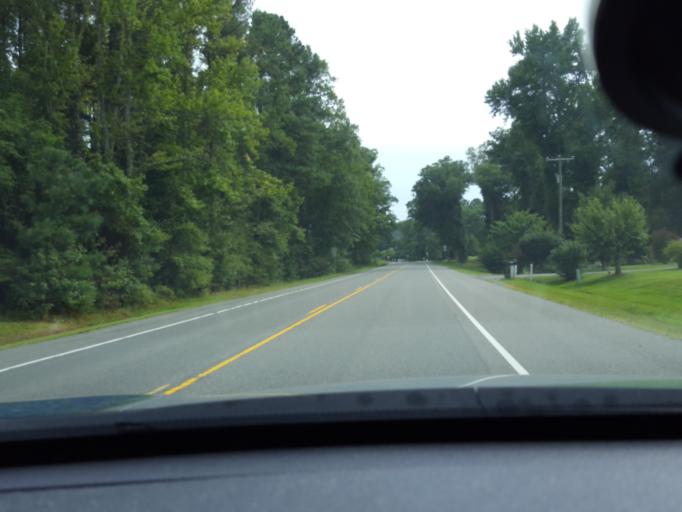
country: US
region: Virginia
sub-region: Hanover County
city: Hanover
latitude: 37.7727
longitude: -77.3711
